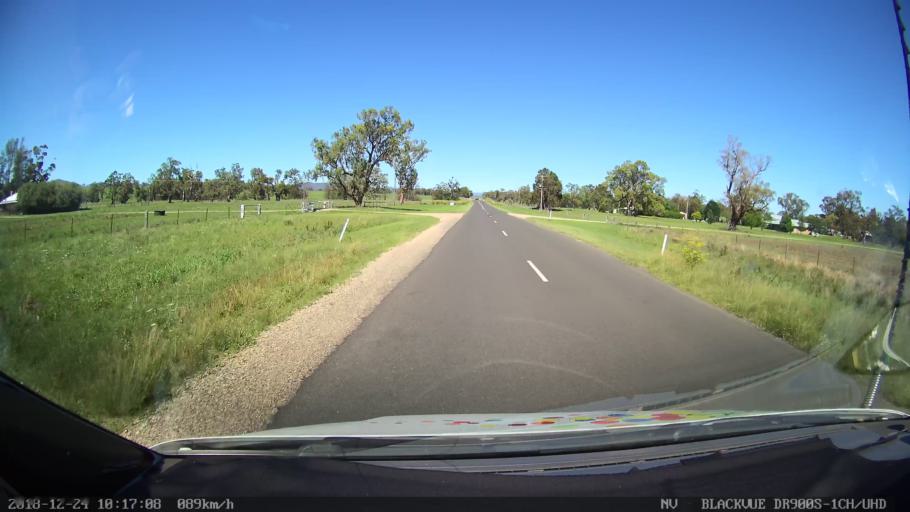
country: AU
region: New South Wales
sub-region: Liverpool Plains
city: Quirindi
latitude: -31.7189
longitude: 150.5958
